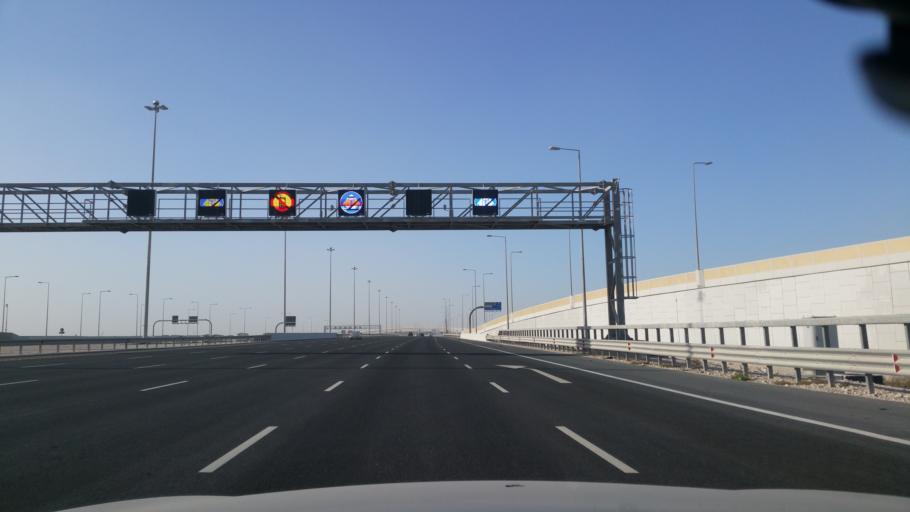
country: QA
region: Al Wakrah
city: Al Wukayr
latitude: 25.1877
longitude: 51.5468
